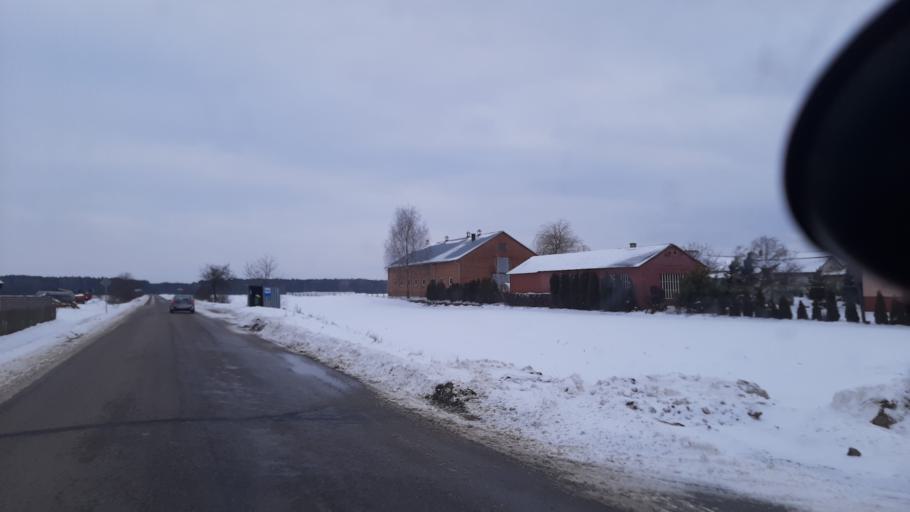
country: PL
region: Lublin Voivodeship
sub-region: Powiat lubartowski
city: Abramow
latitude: 51.4453
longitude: 22.2689
